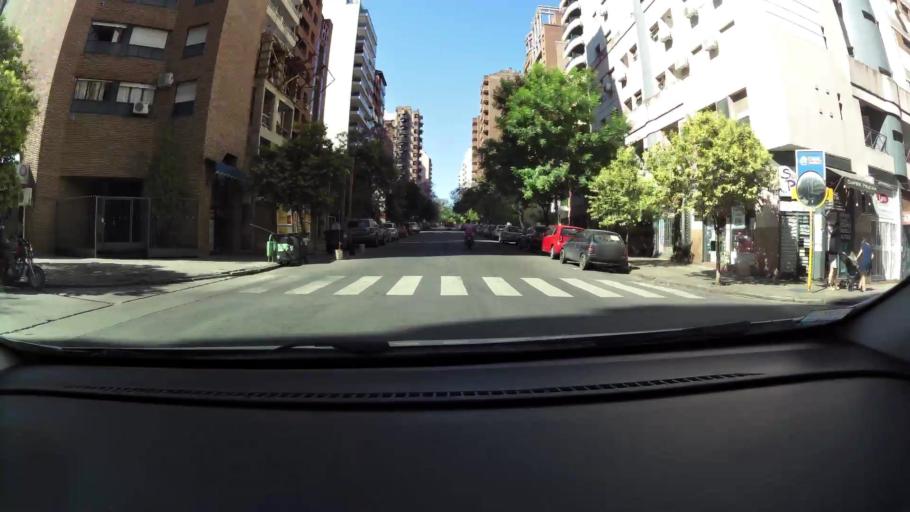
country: AR
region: Cordoba
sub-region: Departamento de Capital
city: Cordoba
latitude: -31.4249
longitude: -64.1817
